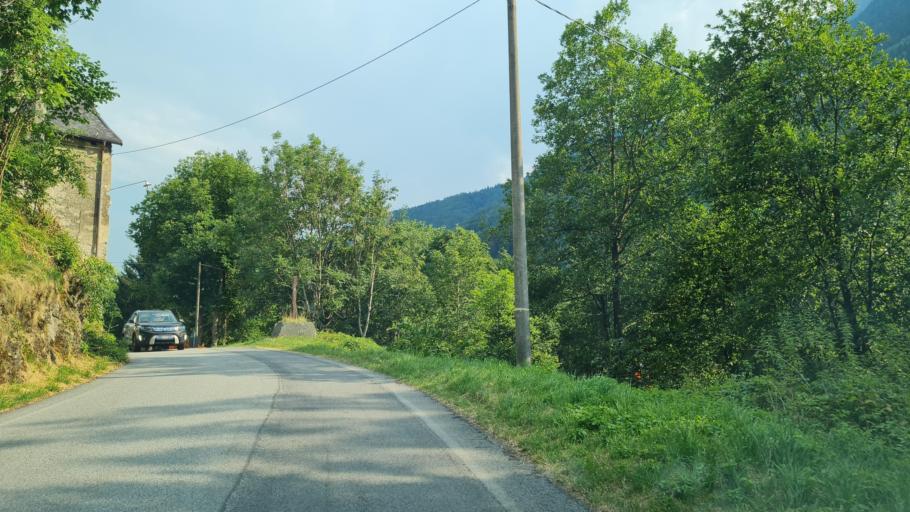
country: IT
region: Piedmont
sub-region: Provincia Verbano-Cusio-Ossola
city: Baceno
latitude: 46.2764
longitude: 8.2970
